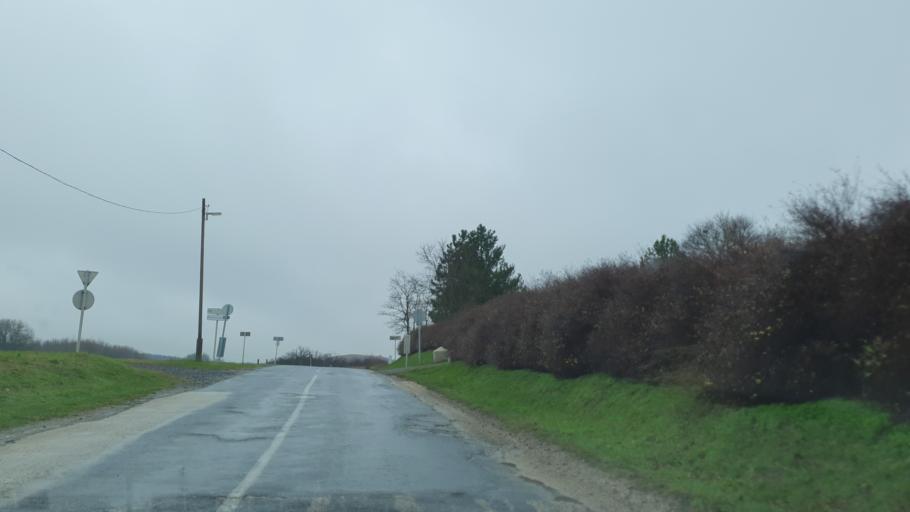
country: HU
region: Veszprem
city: Hajmasker
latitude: 47.1435
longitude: 18.0214
